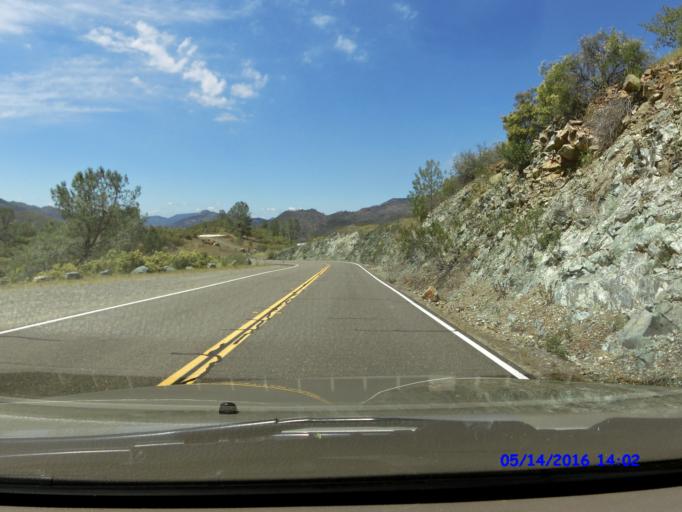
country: US
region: California
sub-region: Mariposa County
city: Mariposa
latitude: 37.5982
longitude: -120.1242
